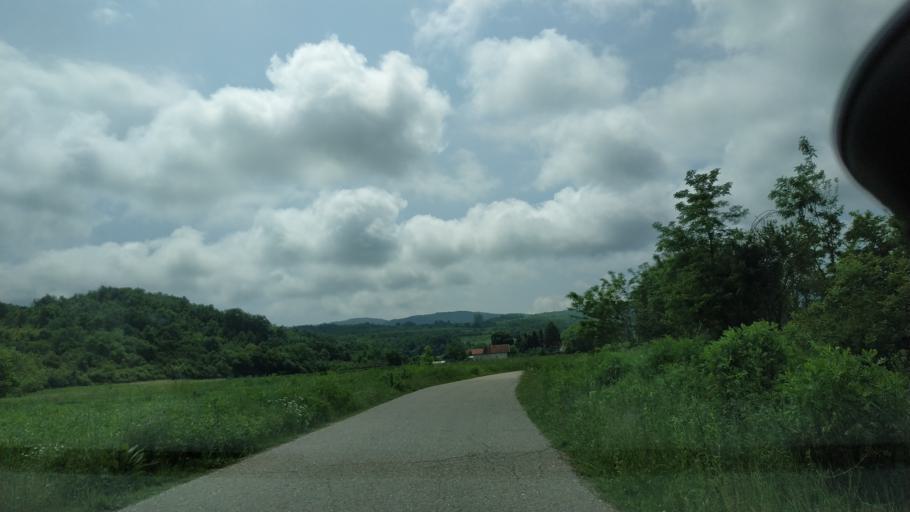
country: RS
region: Central Serbia
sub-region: Nisavski Okrug
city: Aleksinac
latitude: 43.4312
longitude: 21.7112
